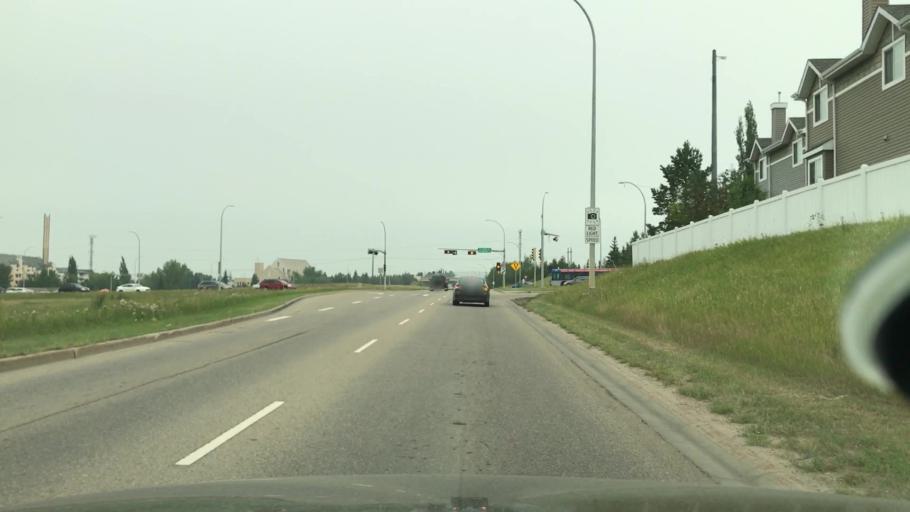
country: CA
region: Alberta
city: Edmonton
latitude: 53.4563
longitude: -113.5885
